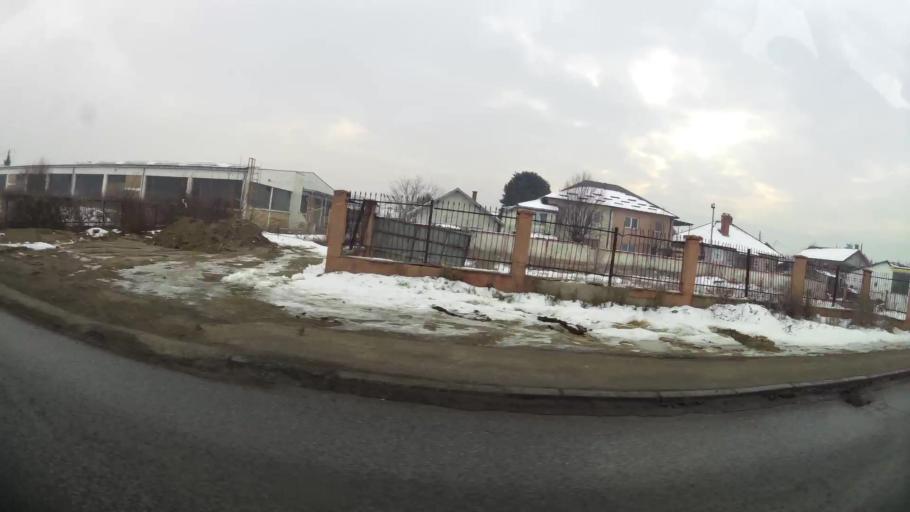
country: MK
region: Saraj
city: Saraj
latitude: 42.0244
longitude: 21.3496
